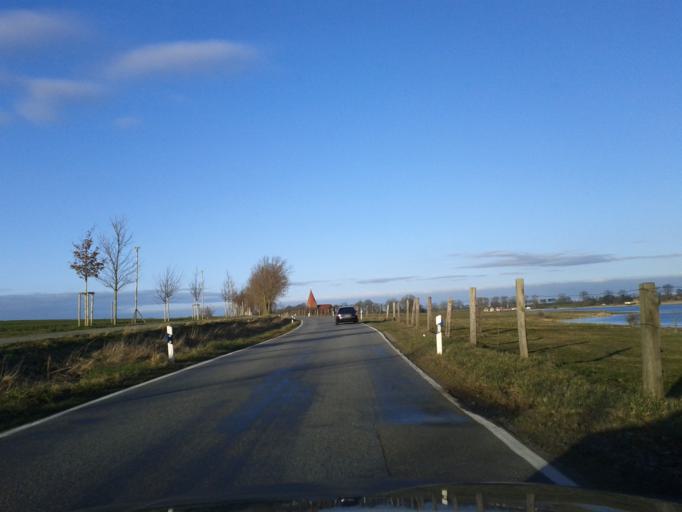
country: DE
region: Mecklenburg-Vorpommern
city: Wismar
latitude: 53.9879
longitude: 11.4287
